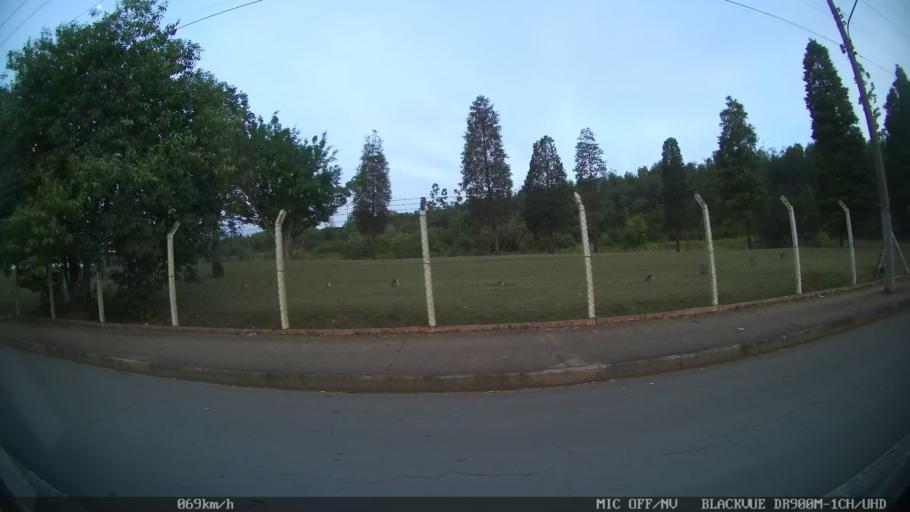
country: BR
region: Sao Paulo
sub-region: Limeira
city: Limeira
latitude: -22.5473
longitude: -47.4249
